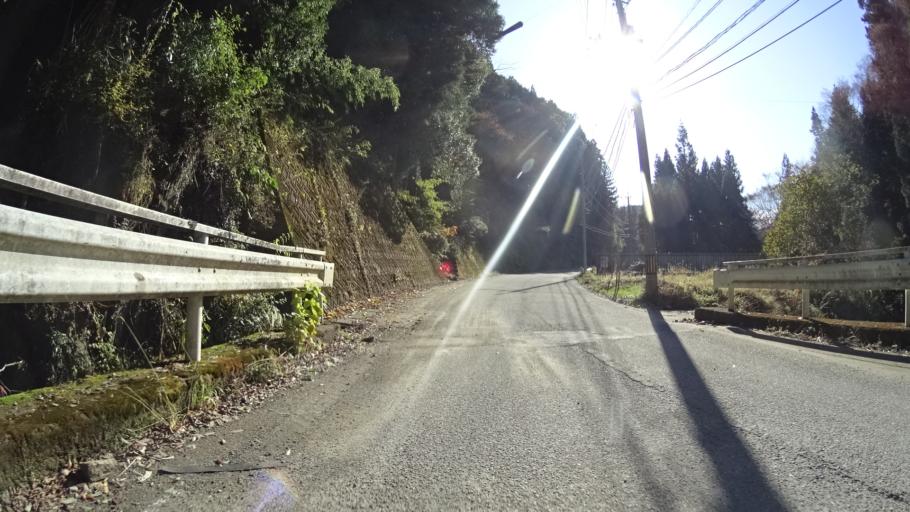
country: JP
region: Yamanashi
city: Uenohara
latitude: 35.6689
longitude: 139.1061
